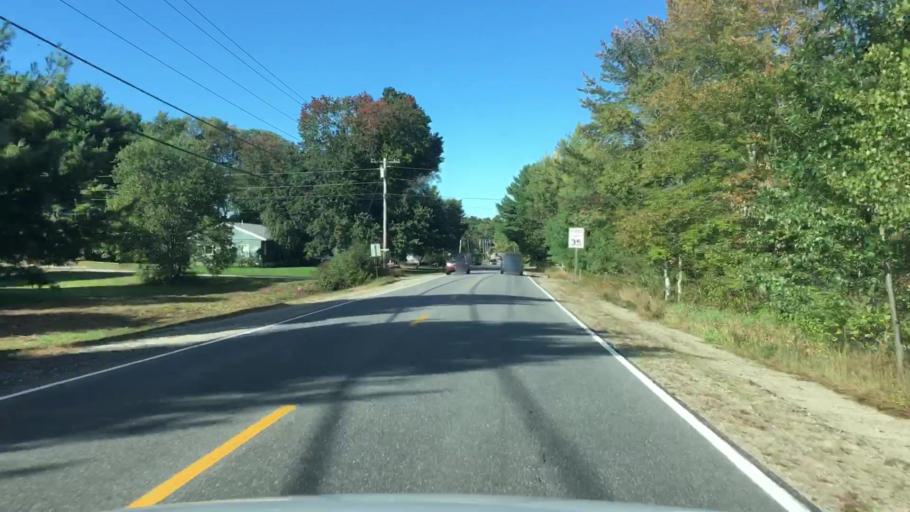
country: US
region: Maine
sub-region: Androscoggin County
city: Lisbon Falls
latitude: 43.9758
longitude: -70.0604
